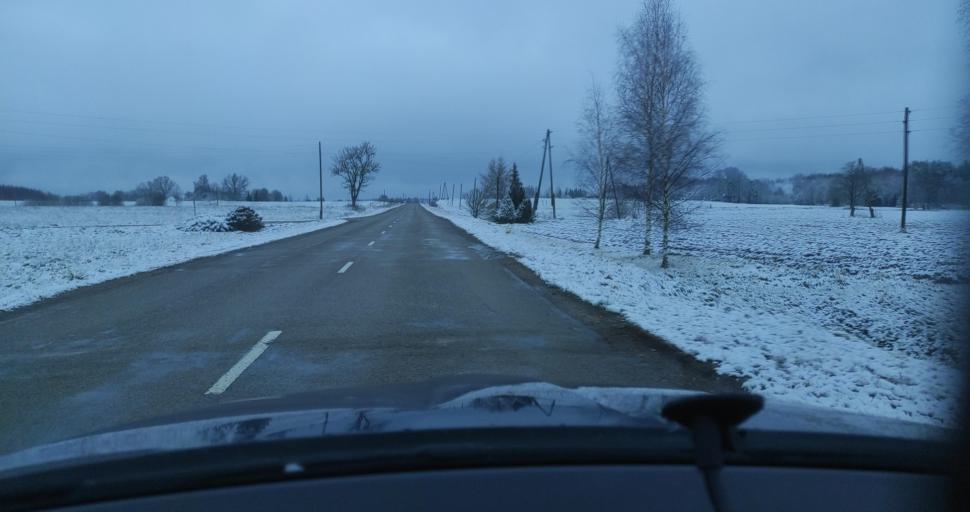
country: LV
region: Skrunda
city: Skrunda
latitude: 56.8788
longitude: 22.2412
